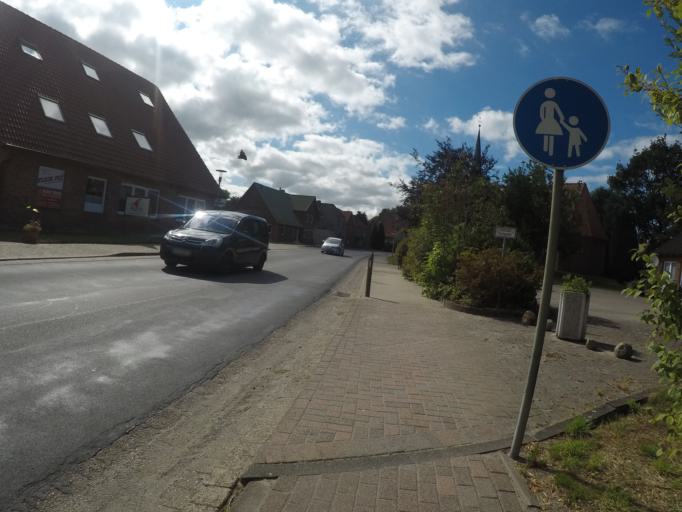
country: DE
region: Lower Saxony
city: Osterbruch
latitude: 53.7776
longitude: 8.9432
